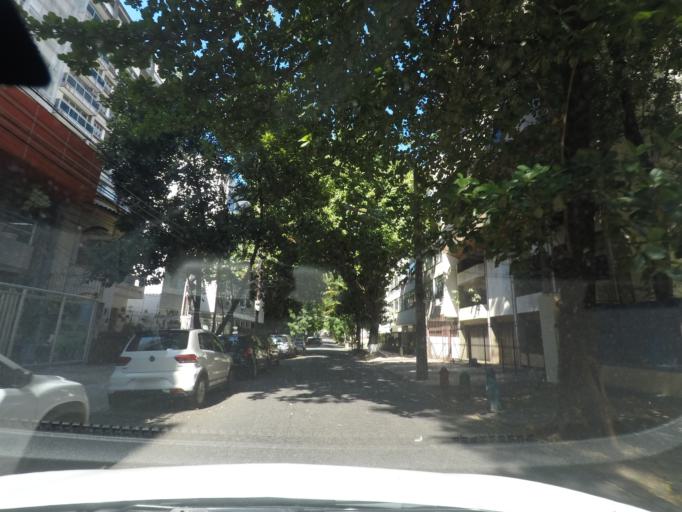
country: BR
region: Rio de Janeiro
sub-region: Rio De Janeiro
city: Rio de Janeiro
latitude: -22.9334
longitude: -43.2397
